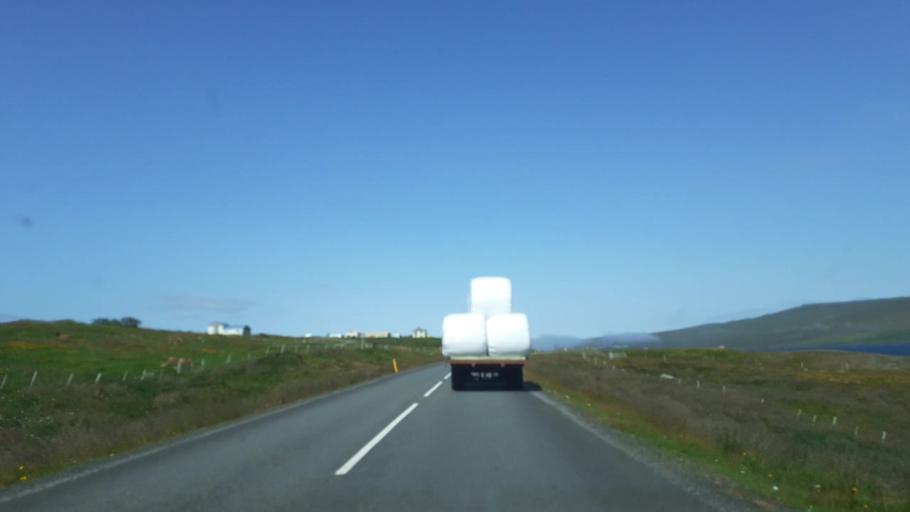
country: IS
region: West
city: Borgarnes
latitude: 65.1790
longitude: -21.0961
